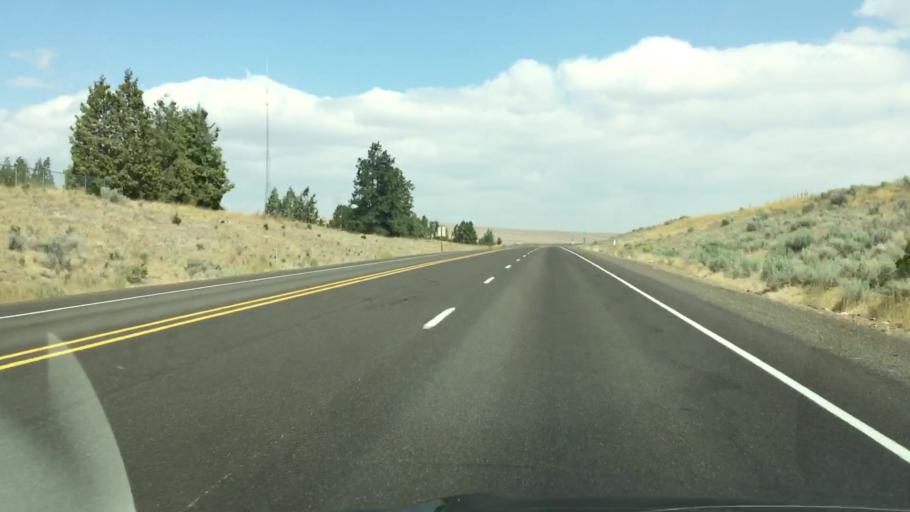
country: US
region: Oregon
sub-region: Wasco County
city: The Dalles
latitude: 45.4559
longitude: -121.1225
